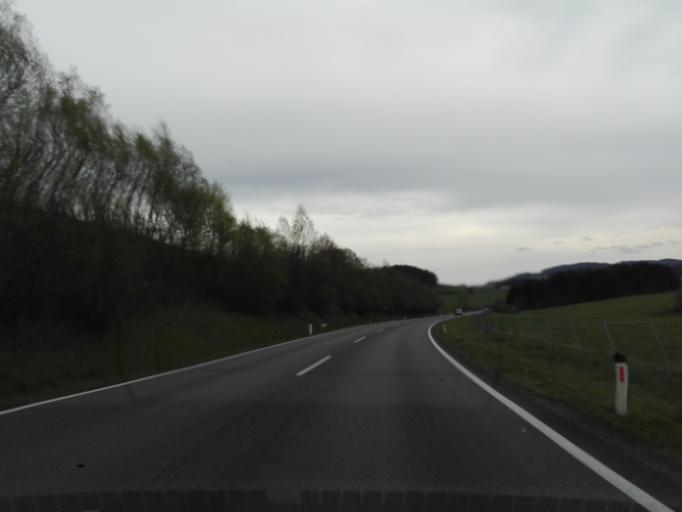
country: AT
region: Upper Austria
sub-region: Politischer Bezirk Rohrbach
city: Schlaegl
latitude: 48.5981
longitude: 13.9628
